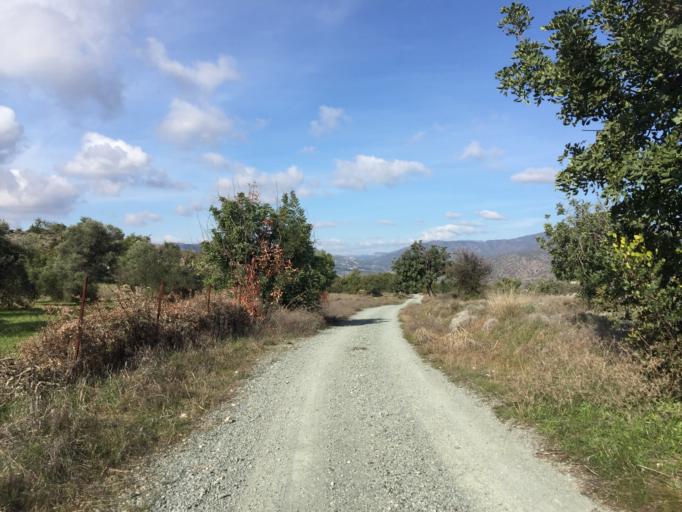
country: CY
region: Larnaka
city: Agios Tychon
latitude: 34.7475
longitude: 33.1257
